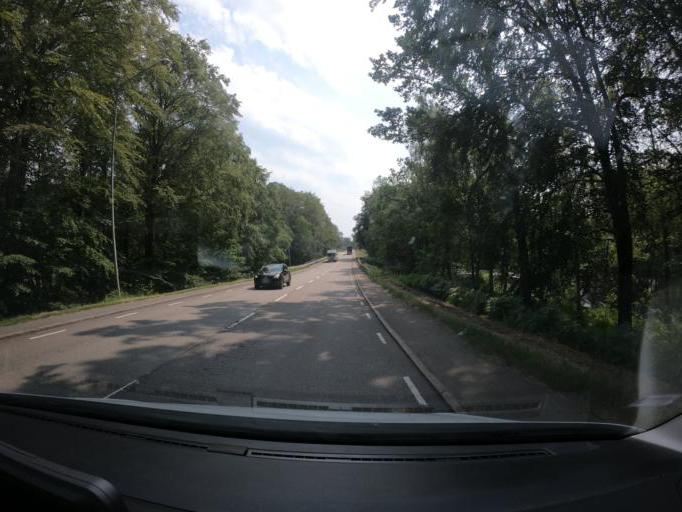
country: SE
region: Skane
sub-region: Hassleholms Kommun
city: Bjarnum
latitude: 56.3532
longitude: 13.6622
